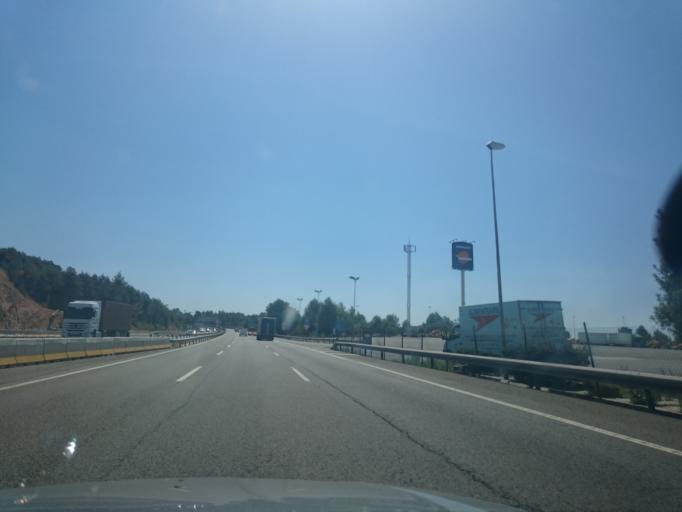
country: ES
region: Catalonia
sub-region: Provincia de Barcelona
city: Castelloli
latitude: 41.5931
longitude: 1.7514
